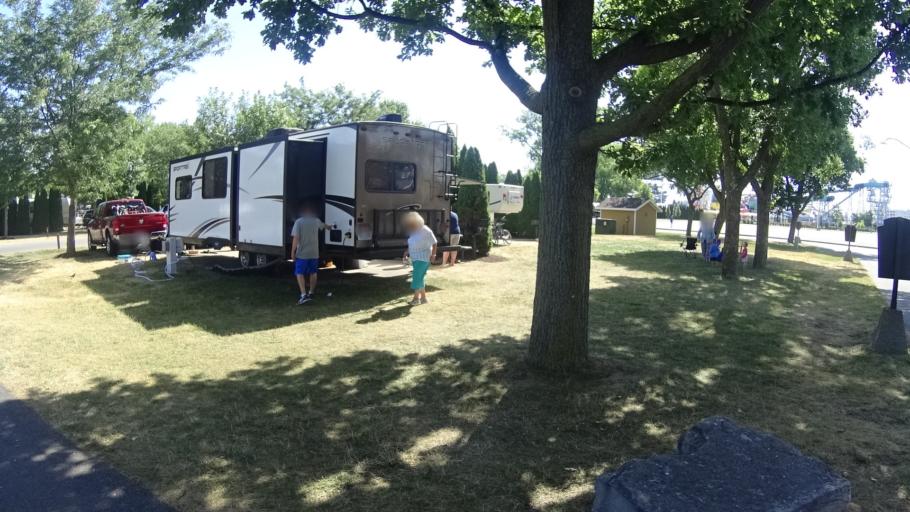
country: US
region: Ohio
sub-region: Erie County
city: Sandusky
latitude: 41.4888
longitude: -82.6902
